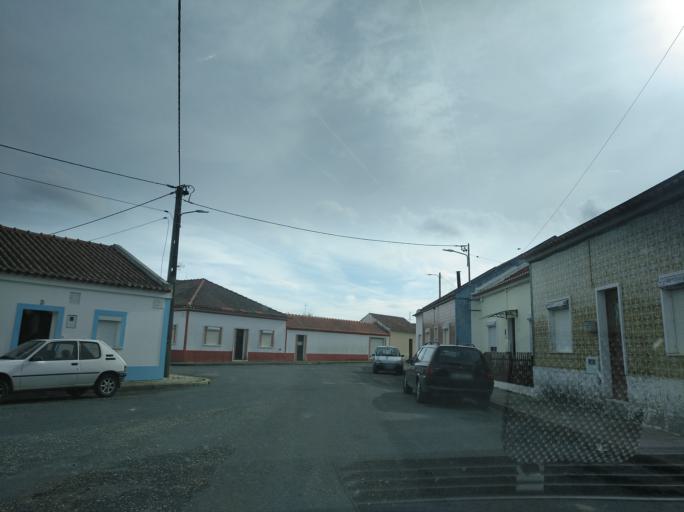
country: PT
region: Setubal
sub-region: Grandola
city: Grandola
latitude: 38.1921
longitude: -8.5550
